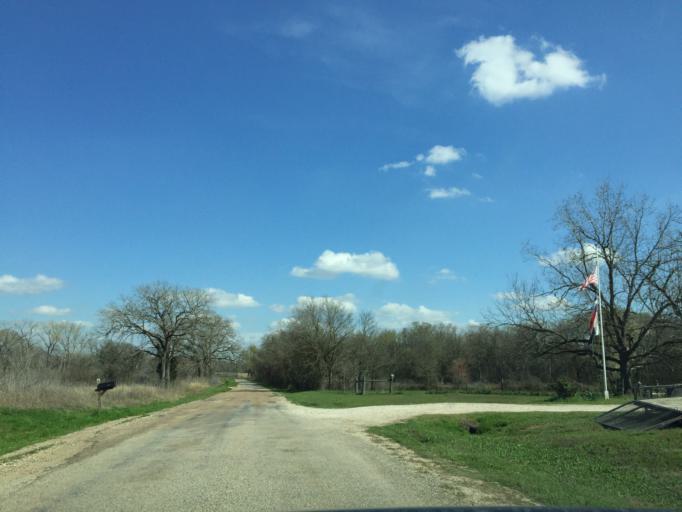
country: US
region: Texas
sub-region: Milam County
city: Thorndale
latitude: 30.5939
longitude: -97.1430
